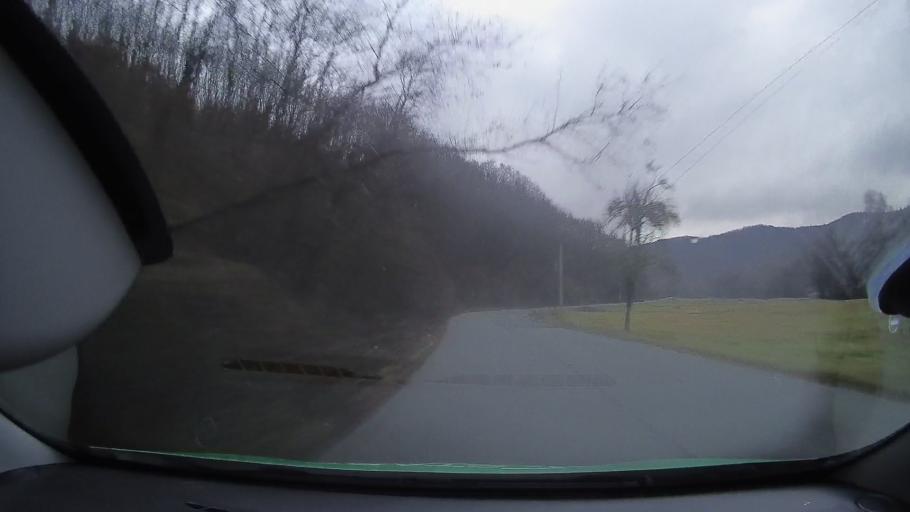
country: RO
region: Hunedoara
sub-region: Comuna Baia de Cris
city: Baia de Cris
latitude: 46.2016
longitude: 22.7181
